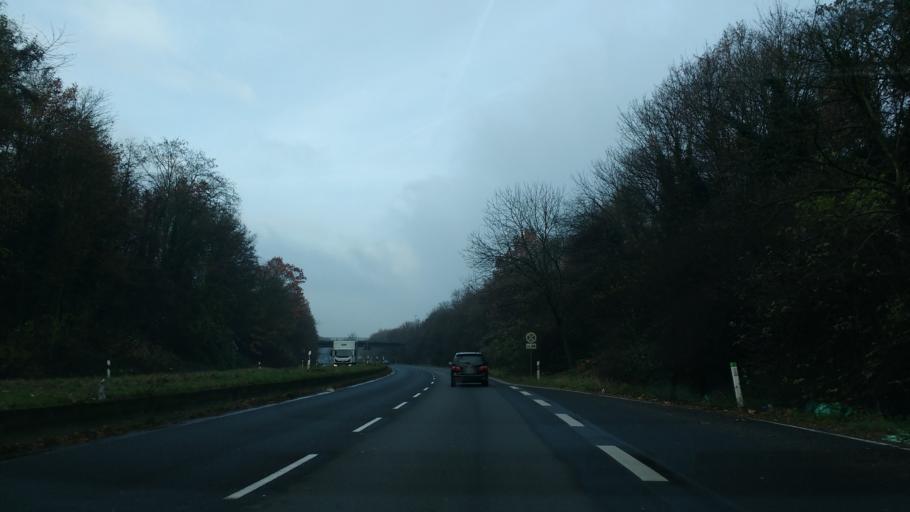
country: DE
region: North Rhine-Westphalia
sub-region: Regierungsbezirk Koln
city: Mengenich
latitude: 50.9410
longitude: 6.8826
